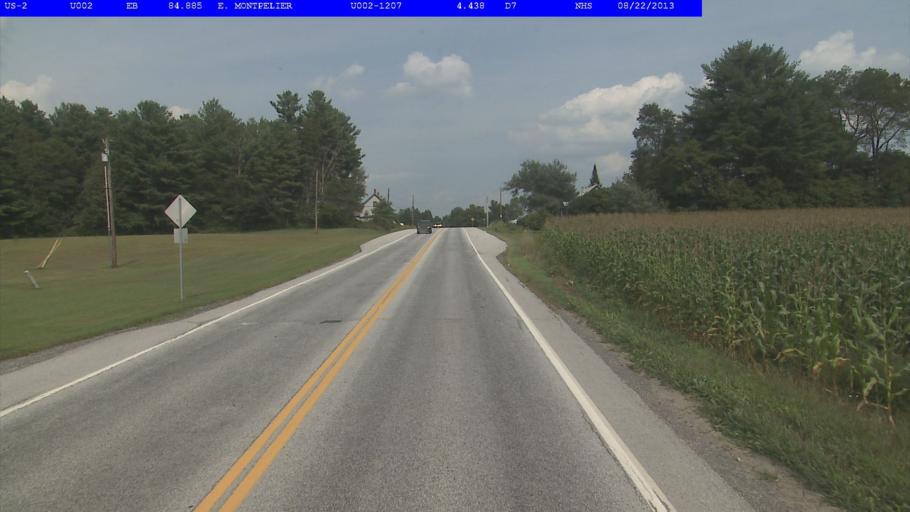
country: US
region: Vermont
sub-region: Washington County
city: Barre
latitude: 44.2699
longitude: -72.4576
